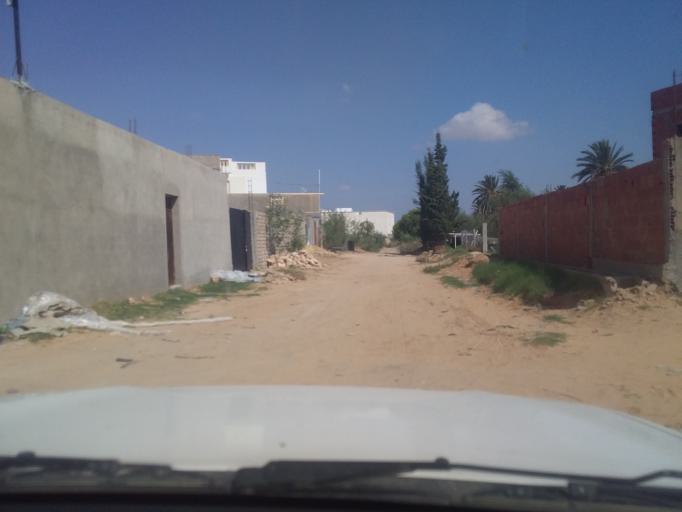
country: TN
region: Qabis
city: Gabes
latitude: 33.6269
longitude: 10.2823
